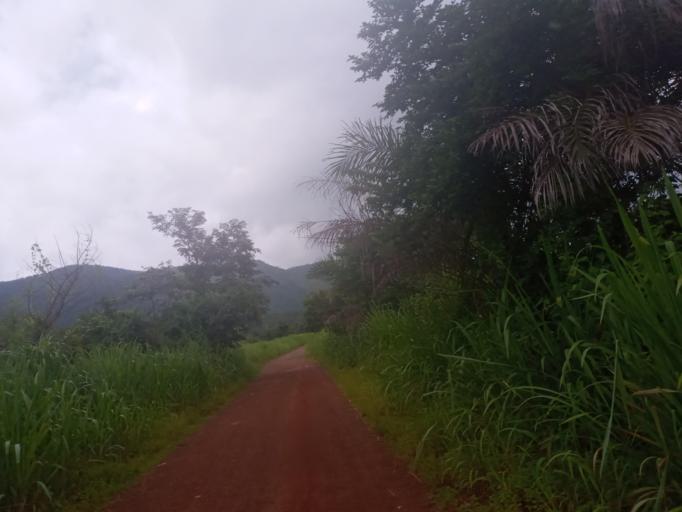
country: SL
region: Northern Province
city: Bumbuna
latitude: 8.9481
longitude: -11.7540
